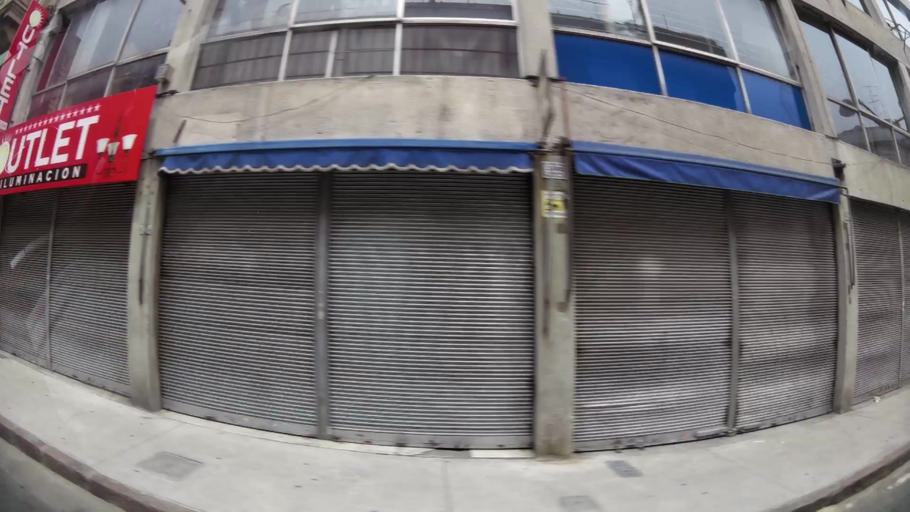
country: UY
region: Montevideo
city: Montevideo
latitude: -34.9081
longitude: -56.2092
